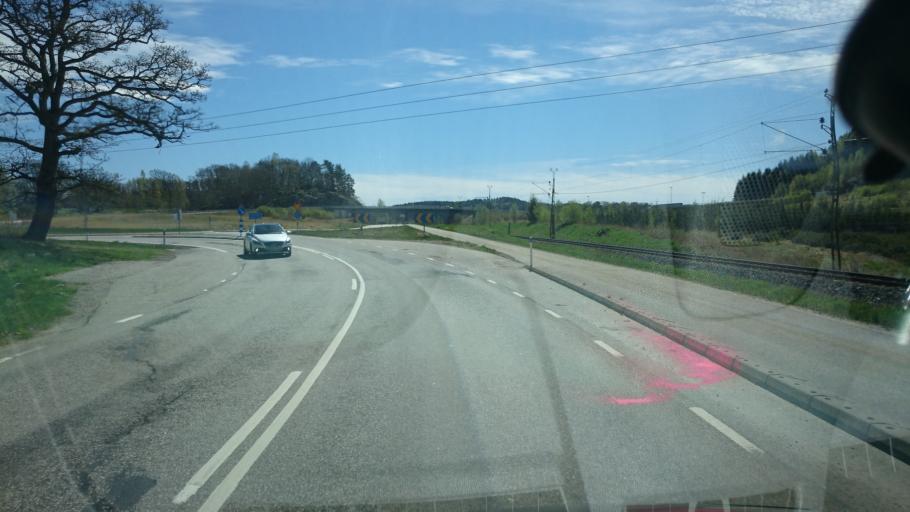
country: SE
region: Vaestra Goetaland
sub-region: Munkedals Kommun
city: Munkedal
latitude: 58.4478
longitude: 11.6951
